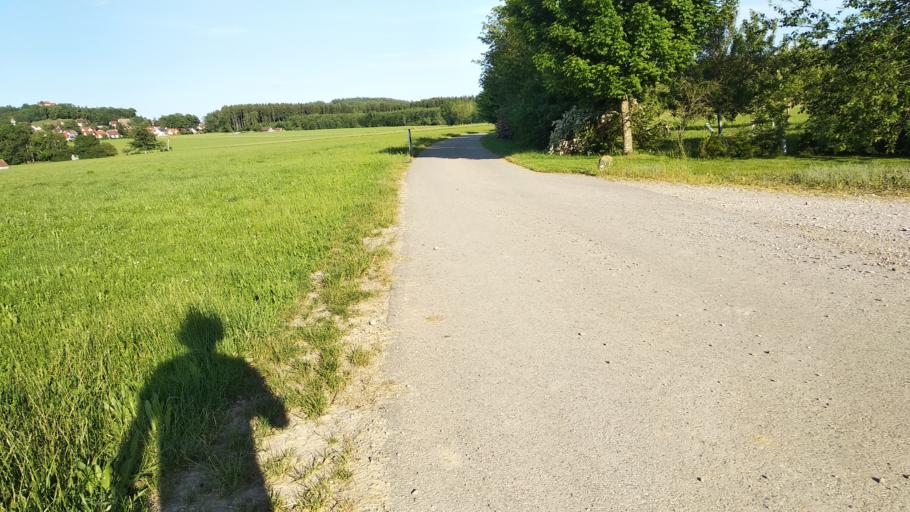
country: DE
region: Bavaria
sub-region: Swabia
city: Kronburg
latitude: 47.9055
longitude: 10.1404
